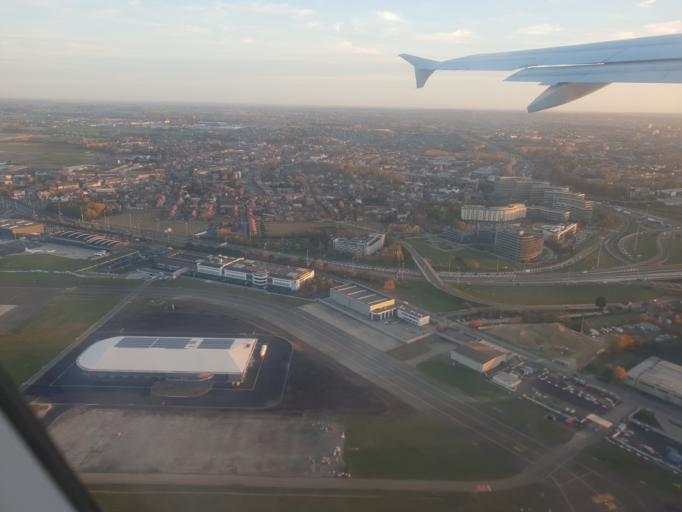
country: BE
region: Flanders
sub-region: Provincie Vlaams-Brabant
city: Machelen
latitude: 50.8997
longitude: 4.4593
